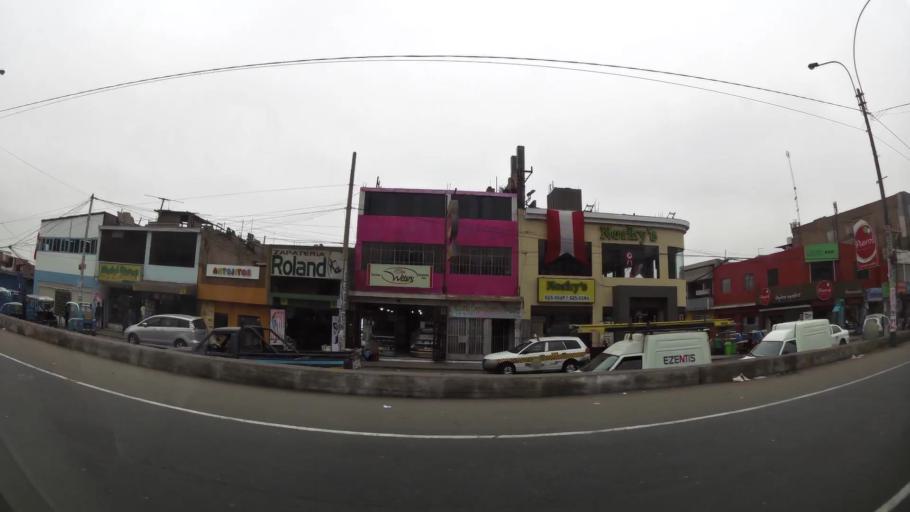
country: PE
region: Lima
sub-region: Lima
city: Independencia
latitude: -11.9574
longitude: -77.0532
